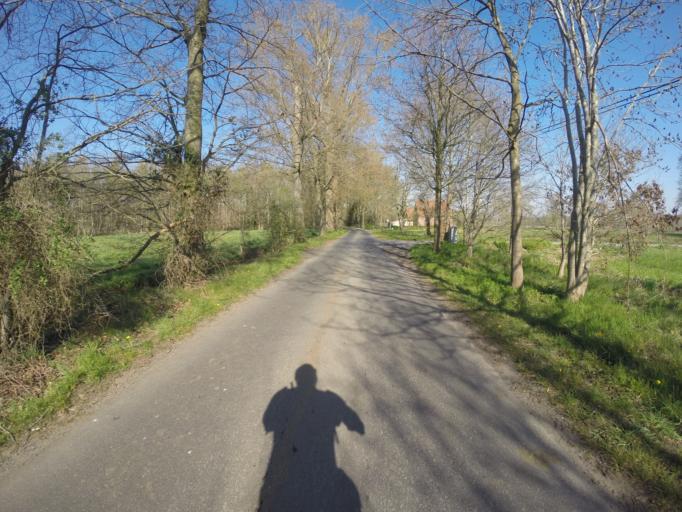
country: BE
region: Flanders
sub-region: Provincie West-Vlaanderen
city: Beernem
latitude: 51.1020
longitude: 3.3670
